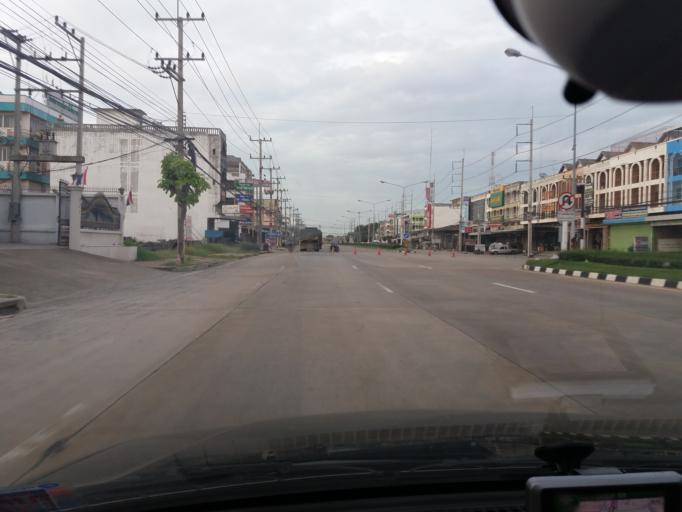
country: TH
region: Suphan Buri
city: U Thong
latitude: 14.3816
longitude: 99.8945
